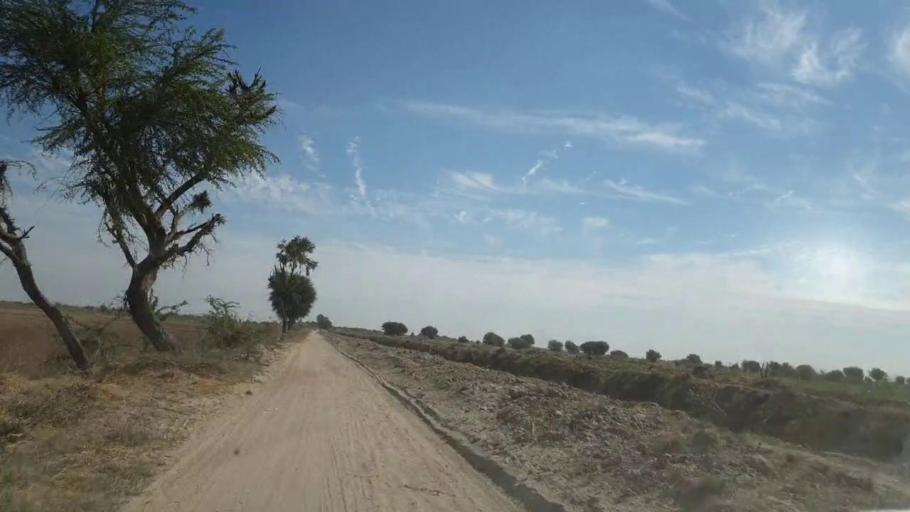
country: PK
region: Sindh
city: Pithoro
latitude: 25.5455
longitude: 69.2984
